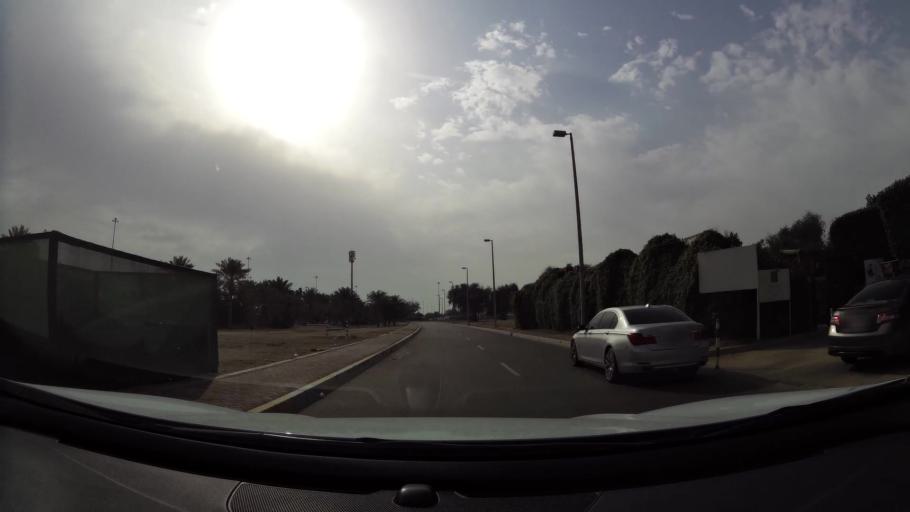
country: AE
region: Abu Dhabi
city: Abu Dhabi
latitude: 24.4751
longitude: 54.3887
